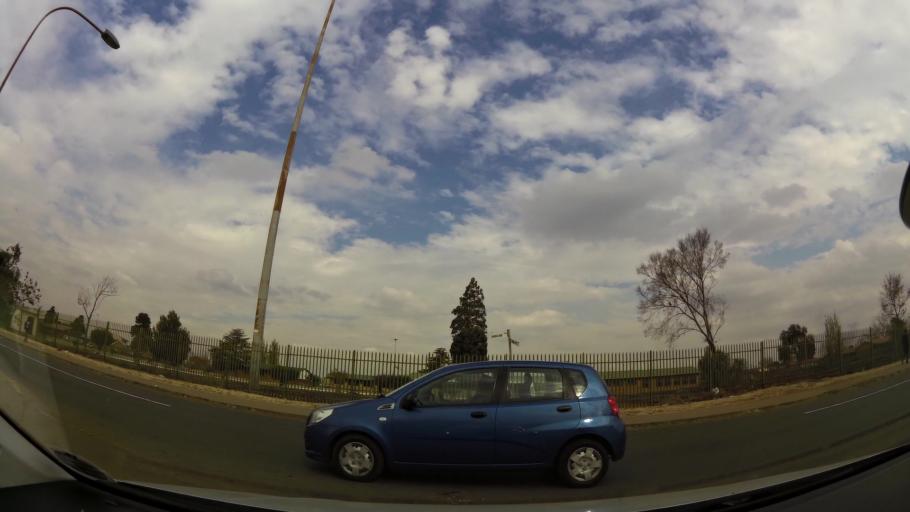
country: ZA
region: Gauteng
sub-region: City of Johannesburg Metropolitan Municipality
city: Soweto
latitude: -26.2727
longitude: 27.8623
